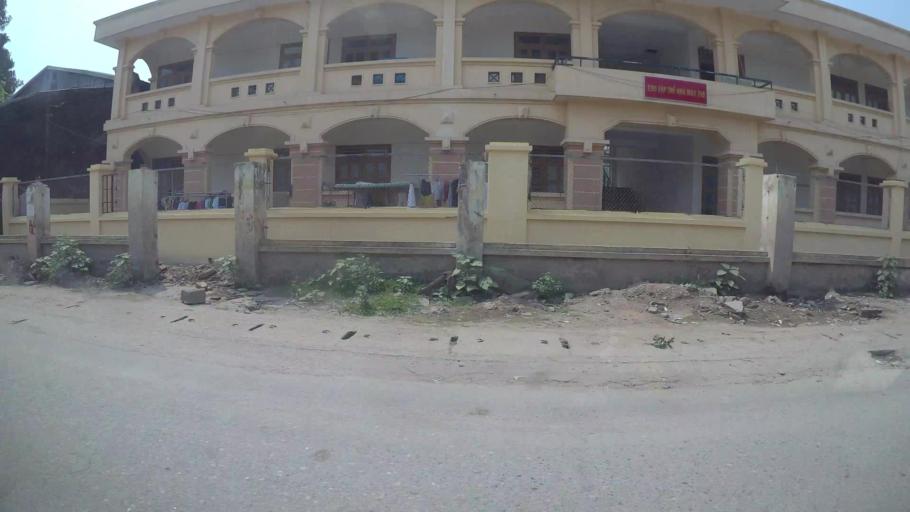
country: VN
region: Ha Noi
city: Ha Dong
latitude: 20.9982
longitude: 105.7637
